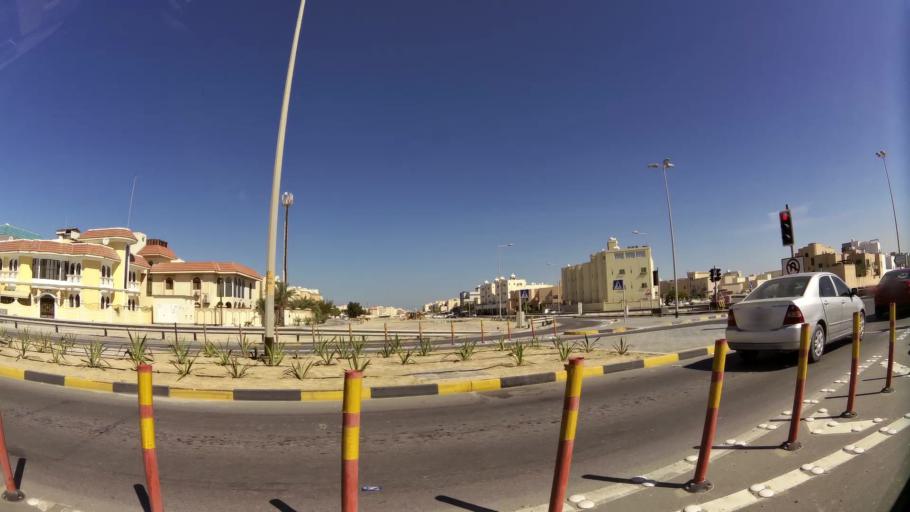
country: BH
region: Muharraq
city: Al Hadd
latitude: 26.2473
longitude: 50.6404
